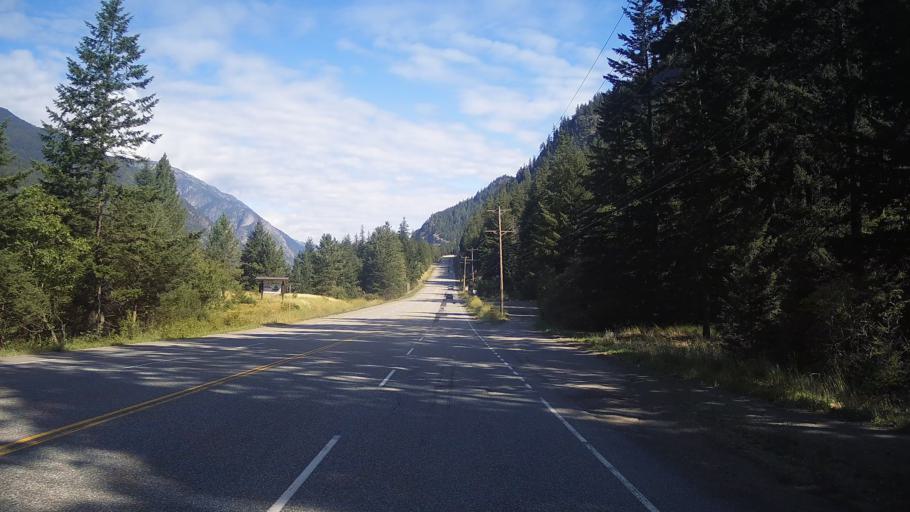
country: CA
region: British Columbia
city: Hope
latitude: 50.0525
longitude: -121.5417
